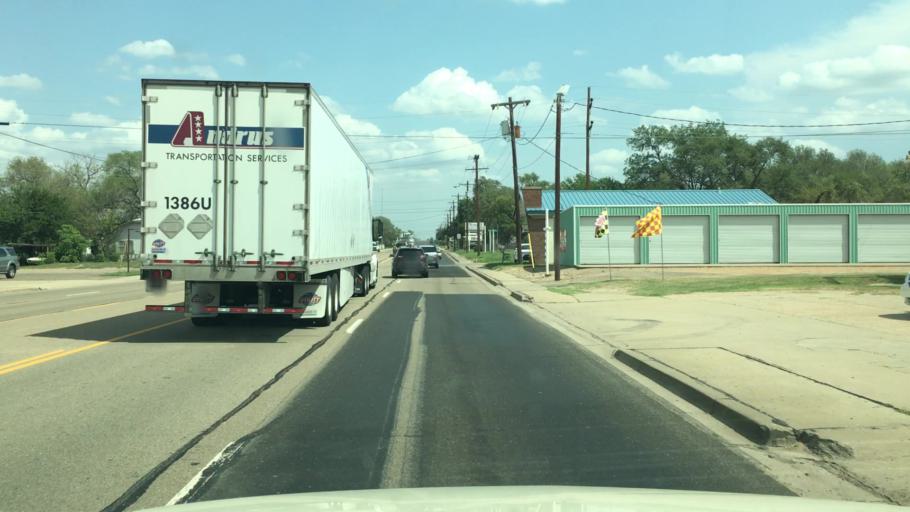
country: US
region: Texas
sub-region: Donley County
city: Clarendon
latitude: 34.9370
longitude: -100.8861
